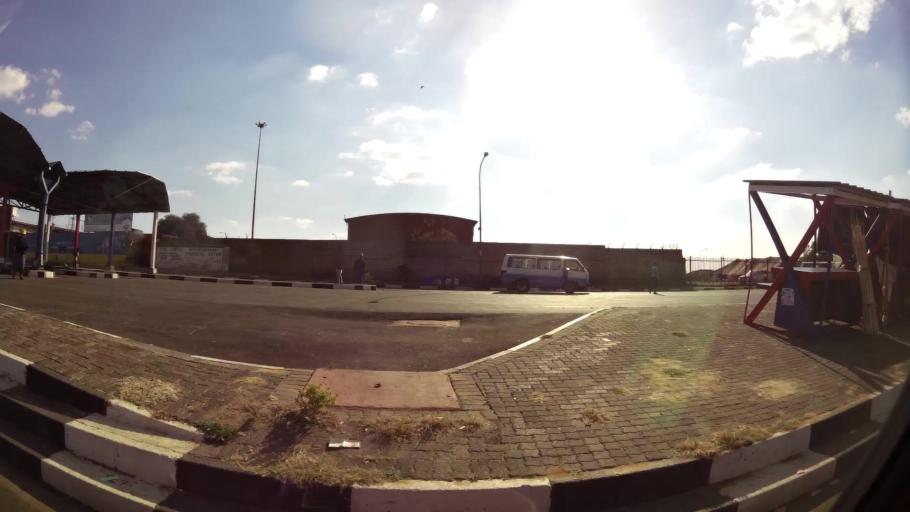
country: ZA
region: Gauteng
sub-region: City of Johannesburg Metropolitan Municipality
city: Soweto
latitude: -26.2297
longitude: 27.8769
